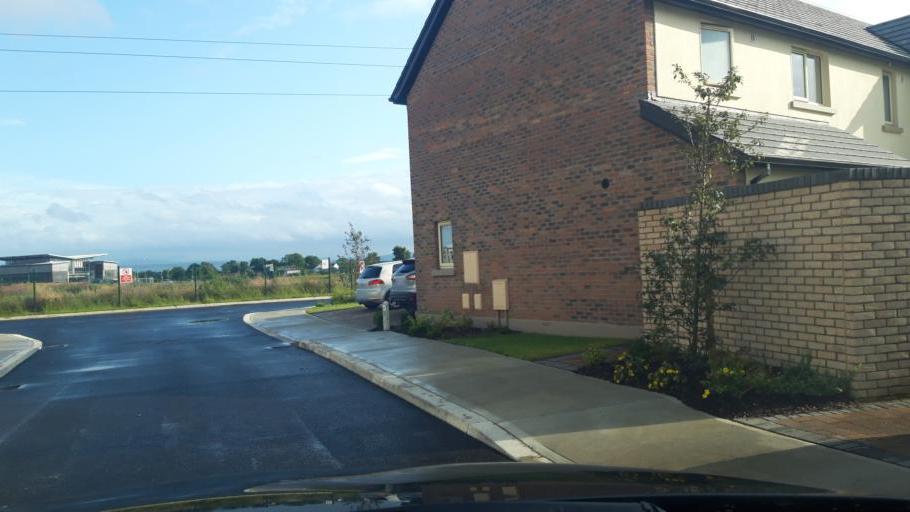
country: IE
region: Leinster
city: Hartstown
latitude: 53.3896
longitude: -6.4435
